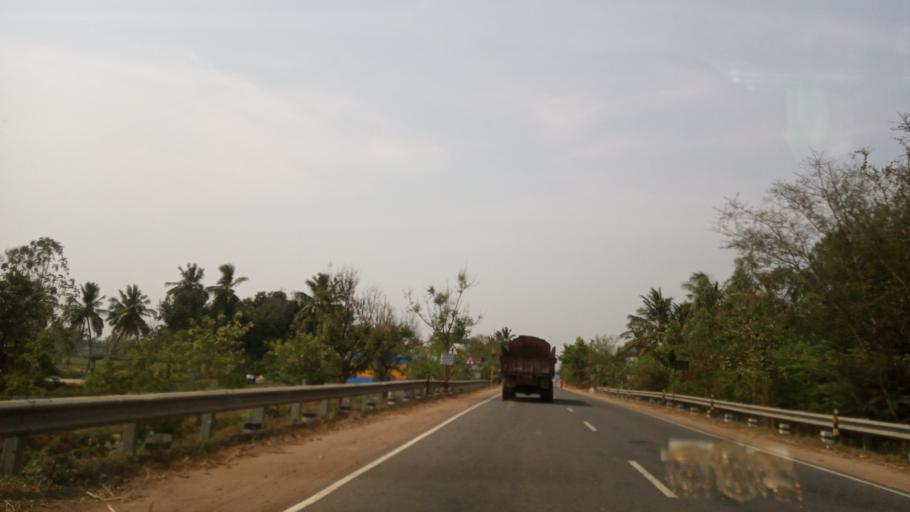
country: IN
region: Tamil Nadu
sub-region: Cuddalore
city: Vriddhachalam
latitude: 11.4507
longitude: 79.3204
